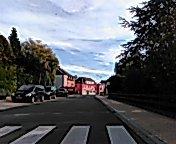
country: LU
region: Luxembourg
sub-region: Canton de Capellen
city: Steinfort
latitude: 49.6458
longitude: 5.9156
